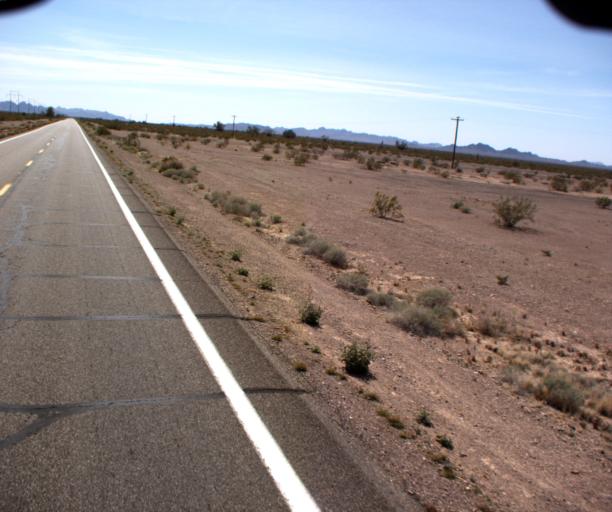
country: US
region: Arizona
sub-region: La Paz County
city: Quartzsite
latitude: 33.4544
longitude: -114.2170
